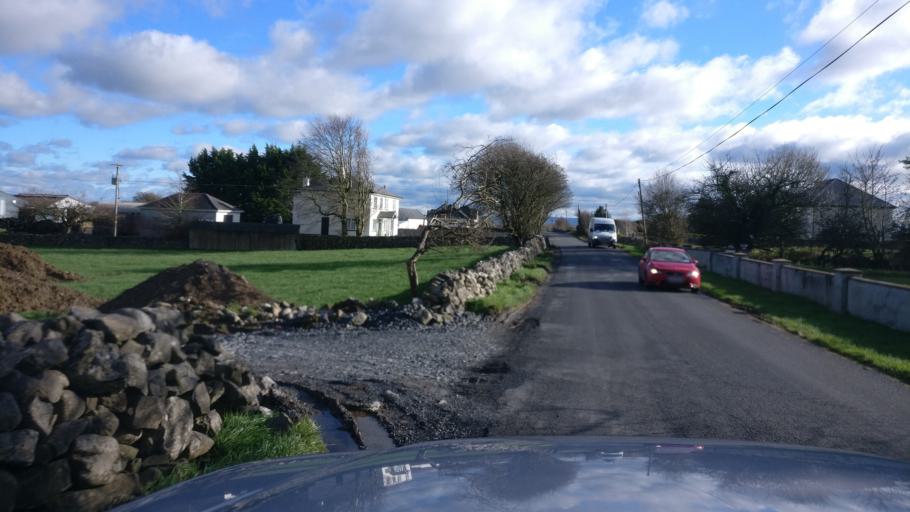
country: IE
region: Connaught
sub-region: County Galway
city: Oranmore
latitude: 53.2595
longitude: -8.8606
